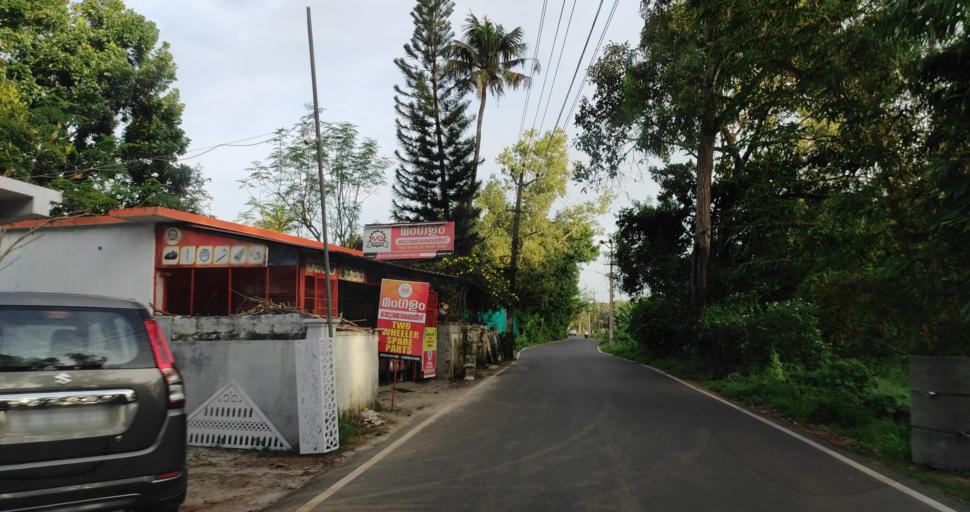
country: IN
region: Kerala
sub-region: Alappuzha
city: Shertallai
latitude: 9.6133
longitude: 76.3322
